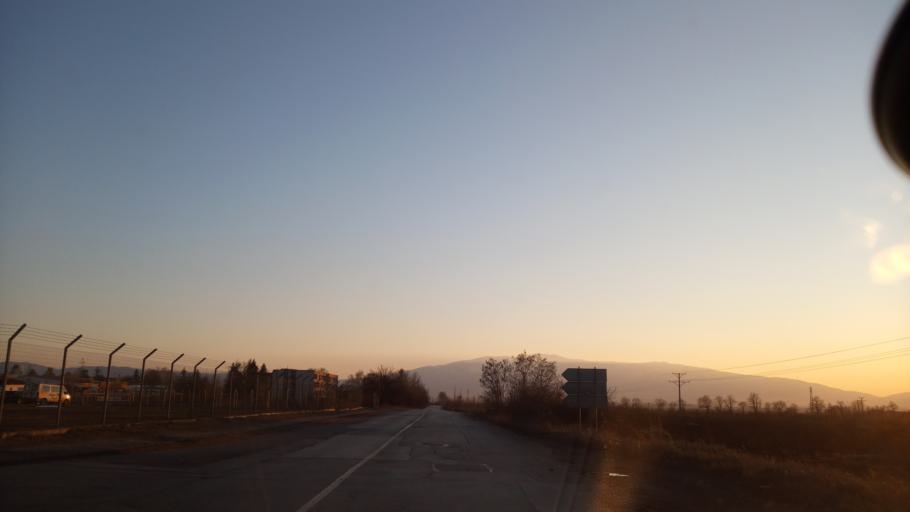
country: BG
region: Sofia-Capital
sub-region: Stolichna Obshtina
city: Bukhovo
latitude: 42.7584
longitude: 23.4861
